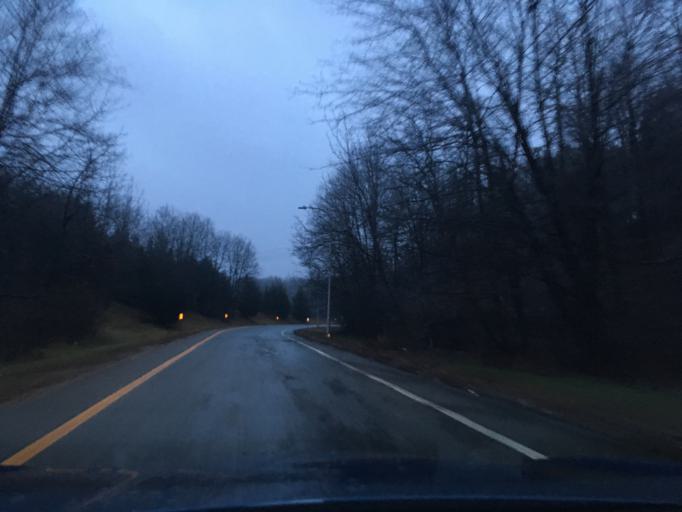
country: US
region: Rhode Island
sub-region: Kent County
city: East Greenwich
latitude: 41.6956
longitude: -71.4783
